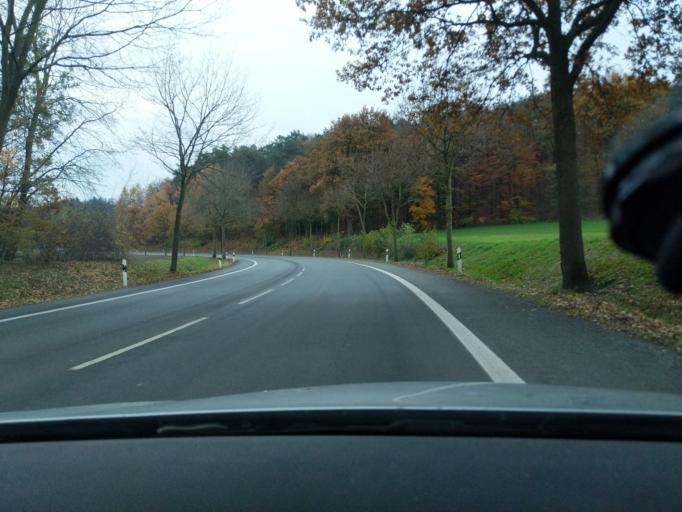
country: DE
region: North Rhine-Westphalia
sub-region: Regierungsbezirk Munster
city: Horstel
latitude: 52.2820
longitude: 7.6014
